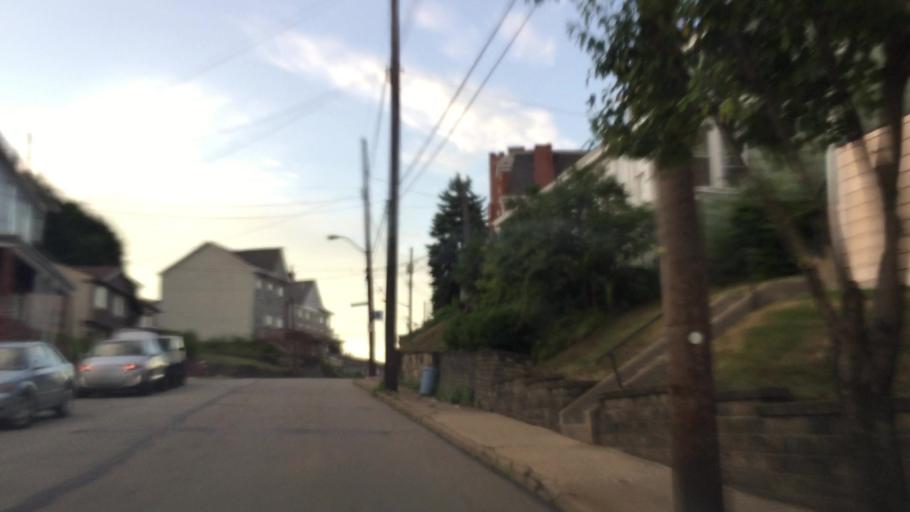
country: US
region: Pennsylvania
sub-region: Allegheny County
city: Pittsburgh
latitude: 40.4271
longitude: -80.0089
